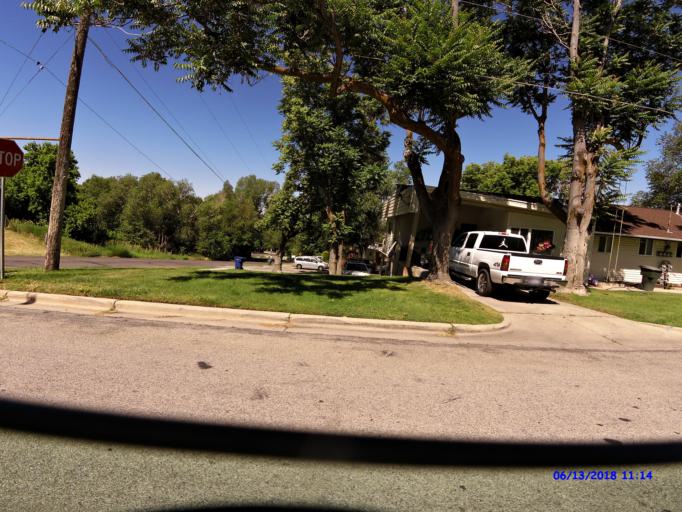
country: US
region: Utah
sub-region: Weber County
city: South Ogden
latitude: 41.2059
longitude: -111.9500
